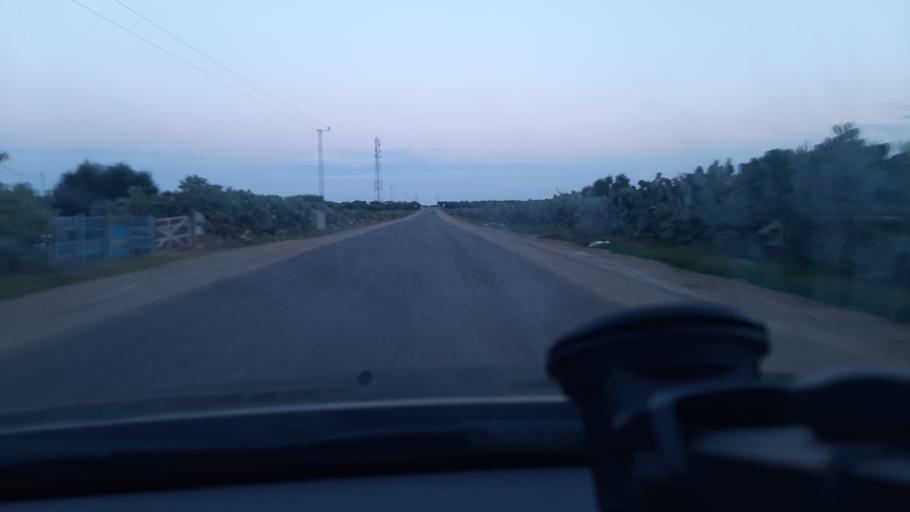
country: TN
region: Al Mahdiyah
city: Shurban
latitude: 35.0179
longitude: 10.4559
